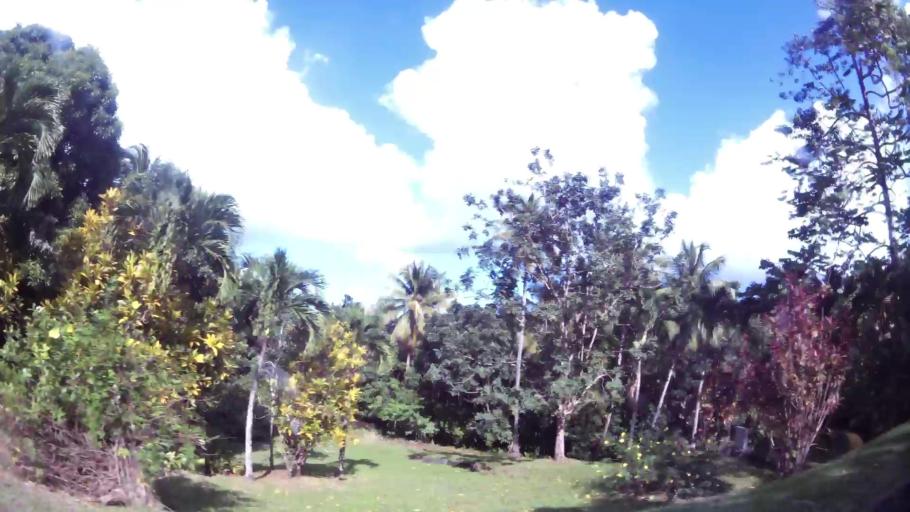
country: DM
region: Saint Andrew
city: Calibishie
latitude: 15.5916
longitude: -61.3729
